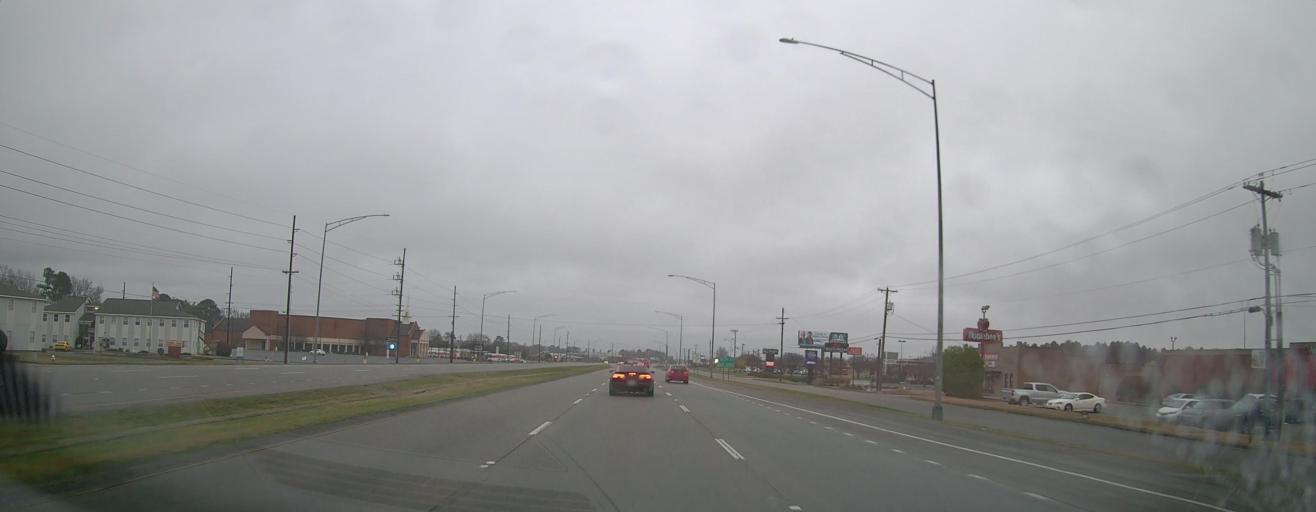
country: US
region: Alabama
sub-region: Morgan County
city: Decatur
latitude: 34.5795
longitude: -87.0203
